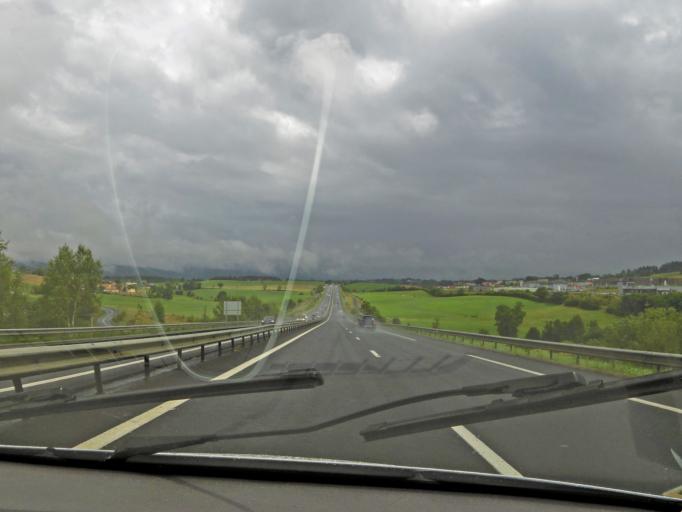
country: FR
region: Auvergne
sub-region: Departement du Cantal
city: Saint-Flour
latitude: 45.0366
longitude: 3.1252
